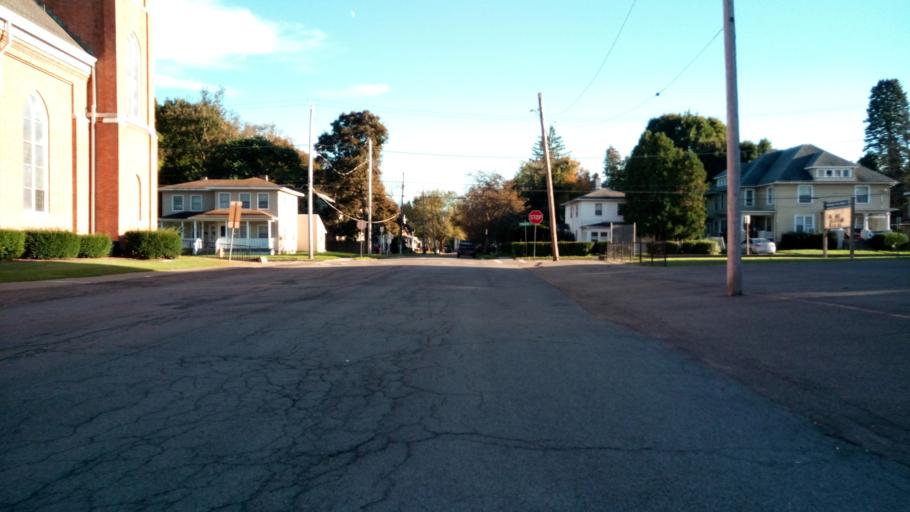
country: US
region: New York
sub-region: Chemung County
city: Elmira
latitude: 42.0771
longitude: -76.8066
